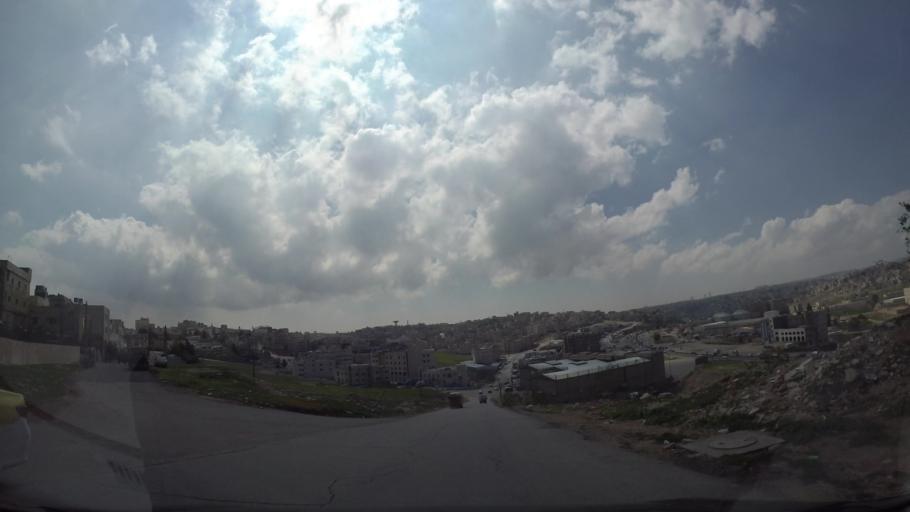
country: JO
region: Zarqa
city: Russeifa
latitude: 31.9966
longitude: 35.9965
